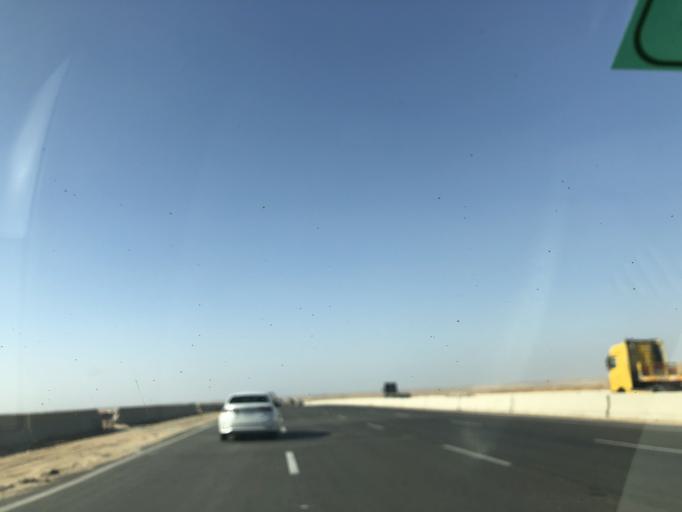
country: EG
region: Al Jizah
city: Madinat Sittah Uktubar
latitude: 30.0269
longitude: 30.8459
